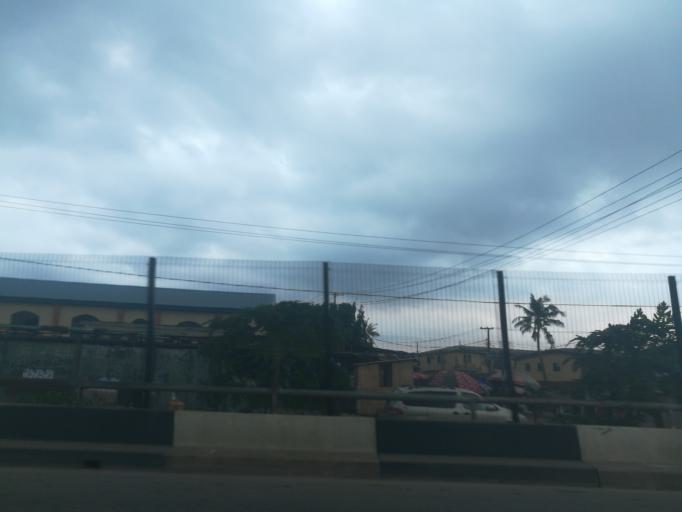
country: NG
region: Lagos
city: Somolu
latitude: 6.5397
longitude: 3.3998
